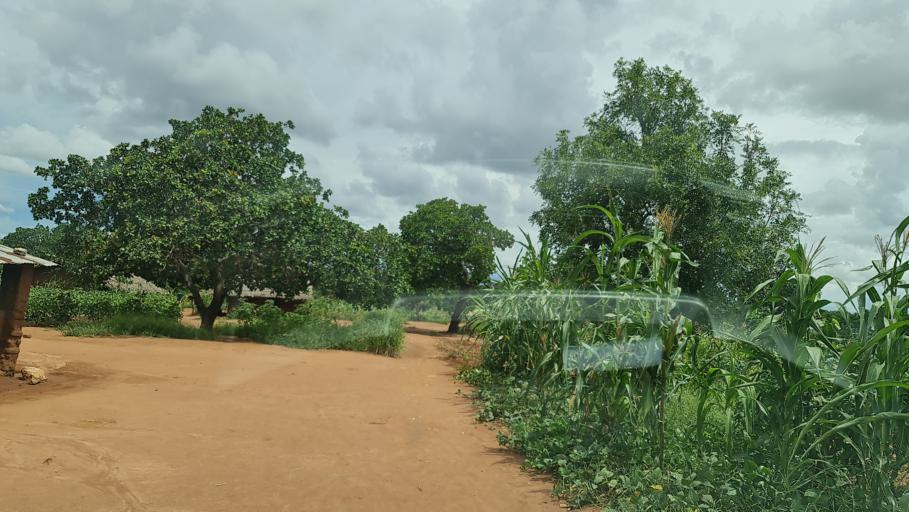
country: MZ
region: Nampula
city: Nacala
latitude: -14.7804
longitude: 39.9960
